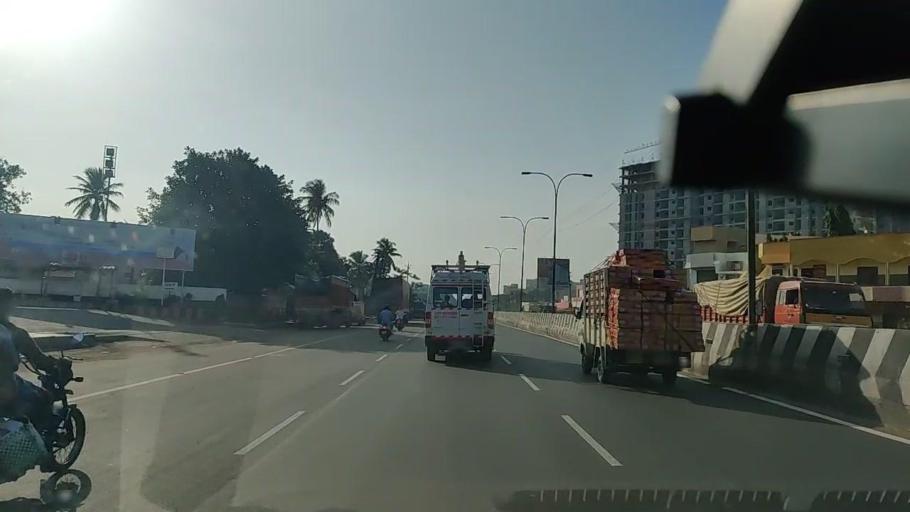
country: IN
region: Tamil Nadu
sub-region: Thiruvallur
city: Chinnasekkadu
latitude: 13.1429
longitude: 80.2224
